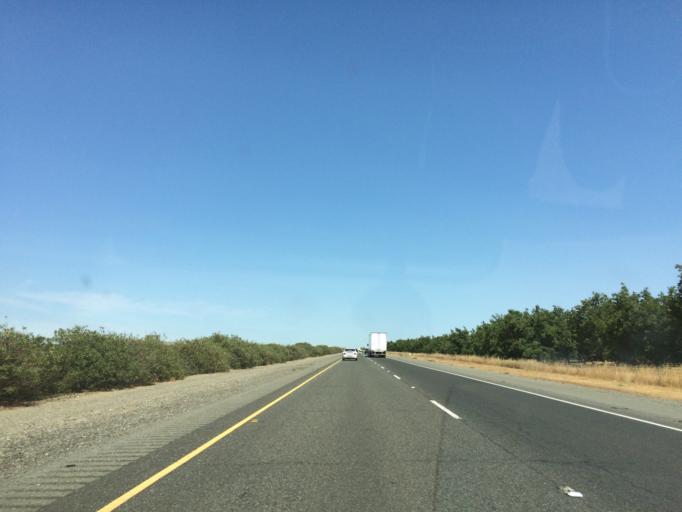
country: US
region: California
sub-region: Glenn County
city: Orland
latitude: 39.6405
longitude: -122.2043
